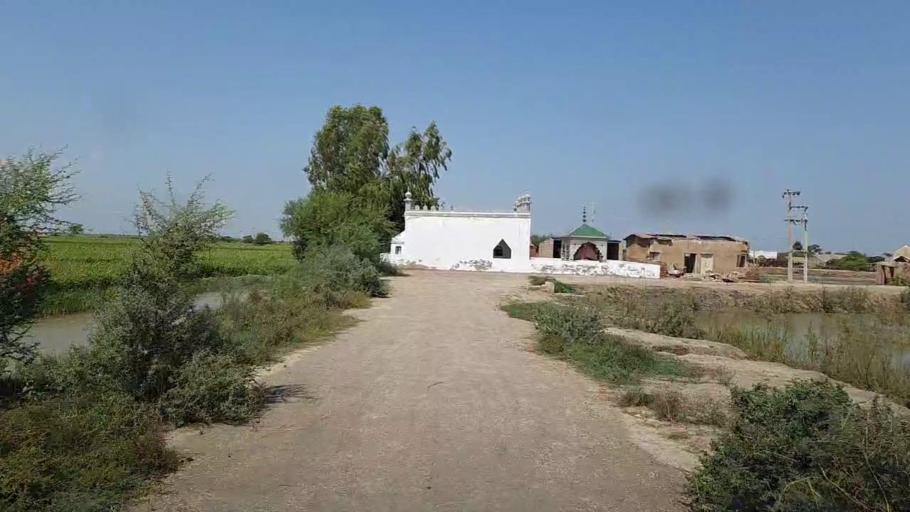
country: PK
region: Sindh
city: Mirpur Batoro
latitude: 24.6443
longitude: 68.4513
